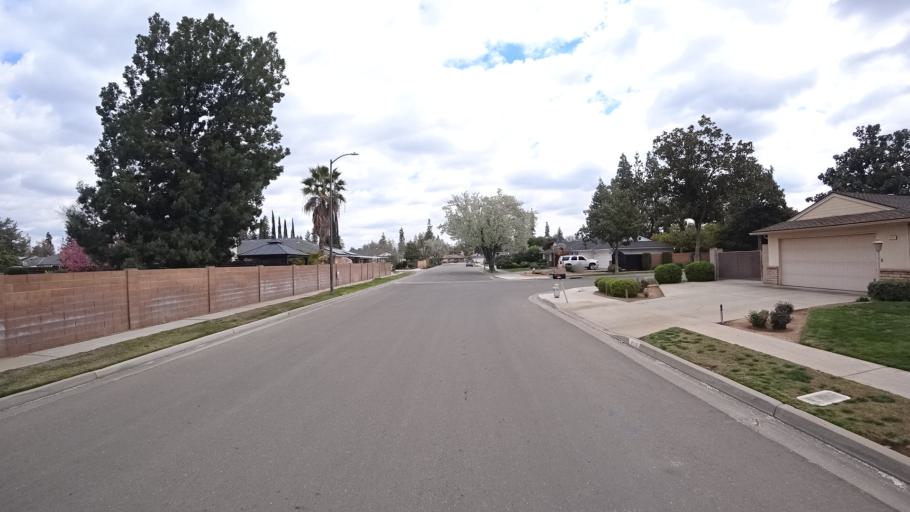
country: US
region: California
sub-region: Fresno County
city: Fresno
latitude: 36.8163
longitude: -119.8470
